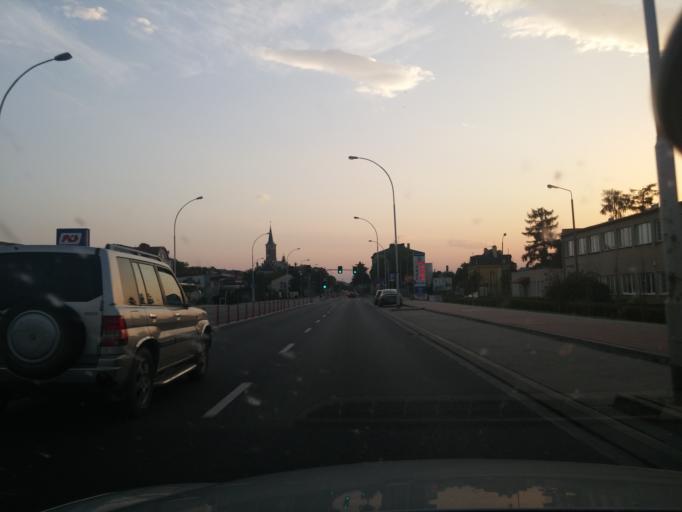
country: PL
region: Subcarpathian Voivodeship
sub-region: Przemysl
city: Przemysl
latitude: 49.7831
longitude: 22.8013
